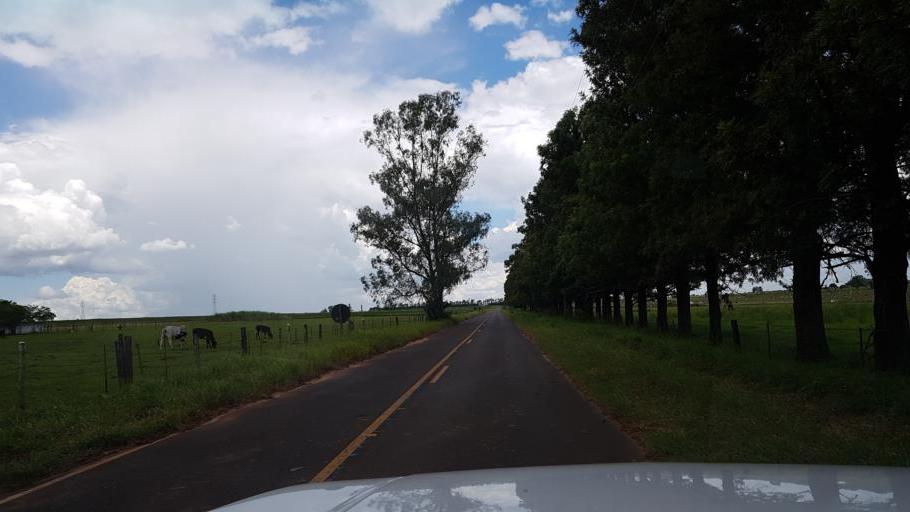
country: BR
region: Sao Paulo
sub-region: Paraguacu Paulista
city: Paraguacu Paulista
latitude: -22.3535
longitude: -50.6245
